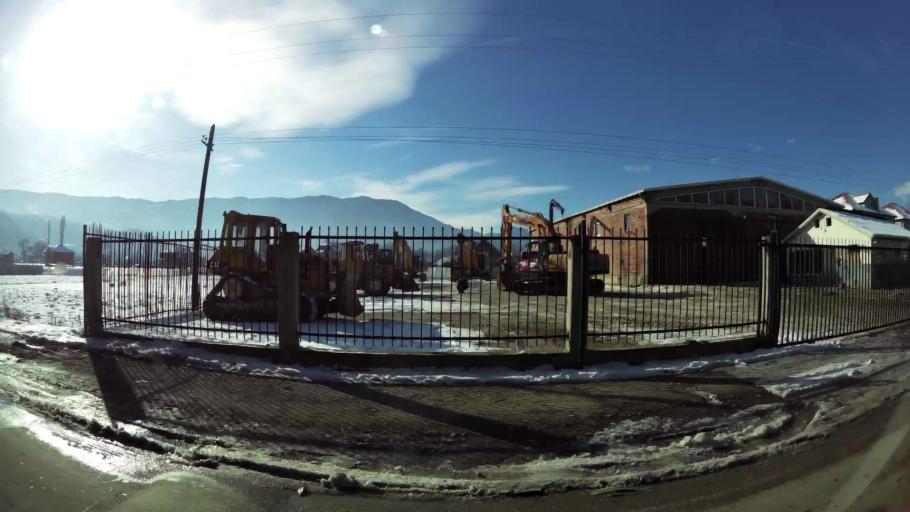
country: MK
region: Saraj
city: Saraj
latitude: 42.0002
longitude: 21.3385
